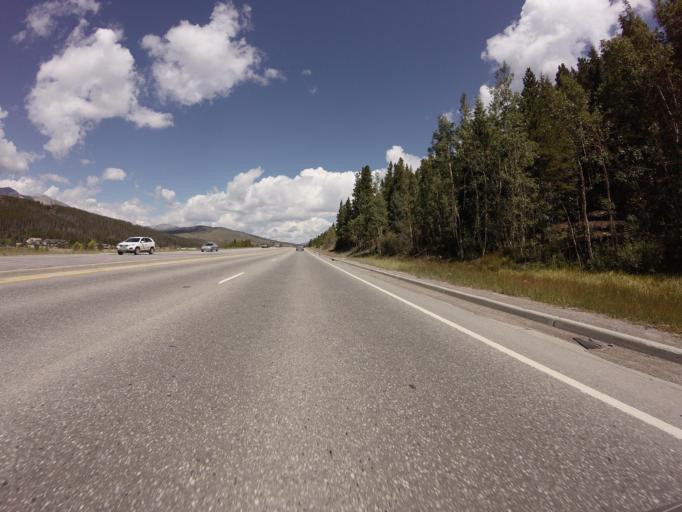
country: US
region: Colorado
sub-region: Summit County
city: Breckenridge
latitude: 39.5017
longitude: -106.0471
